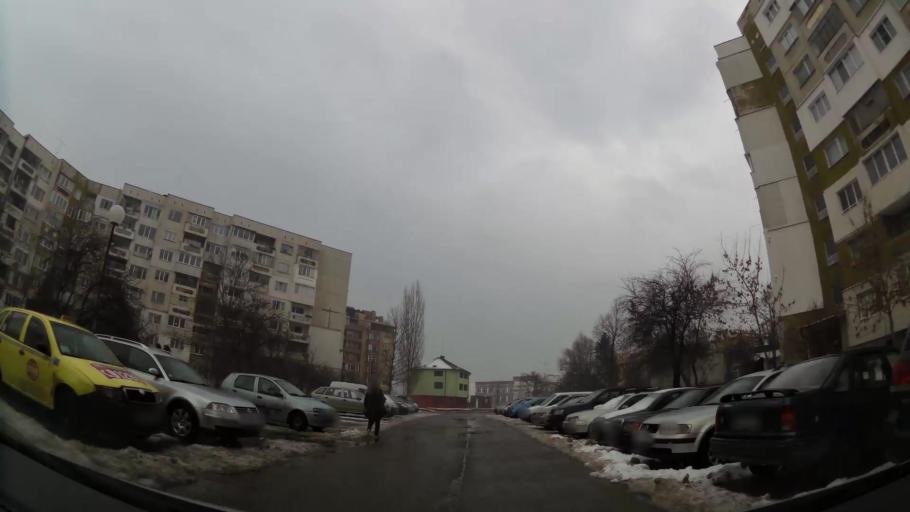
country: BG
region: Sofiya
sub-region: Obshtina Bozhurishte
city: Bozhurishte
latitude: 42.6877
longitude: 23.2458
